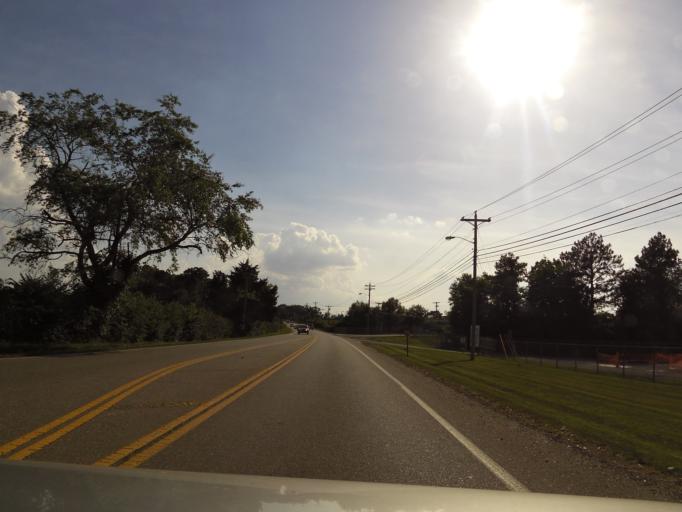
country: US
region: Tennessee
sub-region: Blount County
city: Alcoa
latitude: 35.8061
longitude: -83.9735
